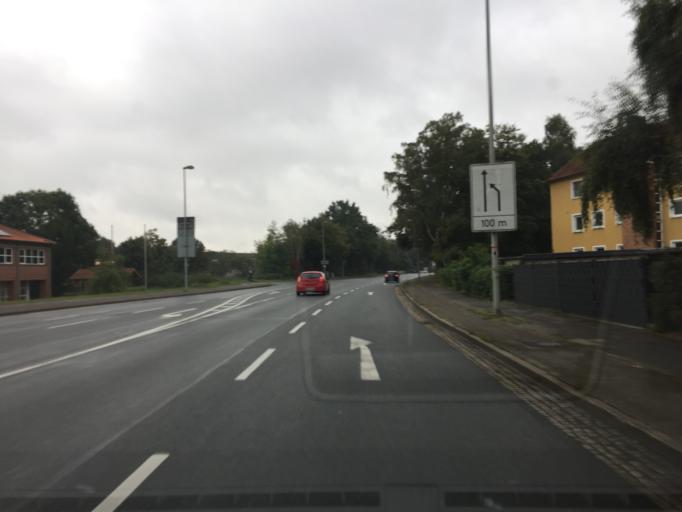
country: DE
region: Lower Saxony
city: Nienburg
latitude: 52.6413
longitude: 9.2192
